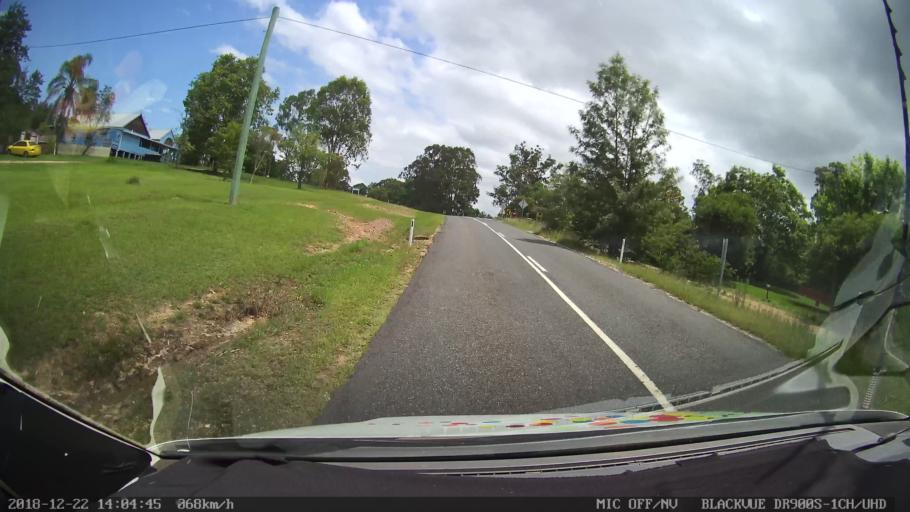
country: AU
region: New South Wales
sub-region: Clarence Valley
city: Coutts Crossing
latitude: -29.9377
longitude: 152.7268
